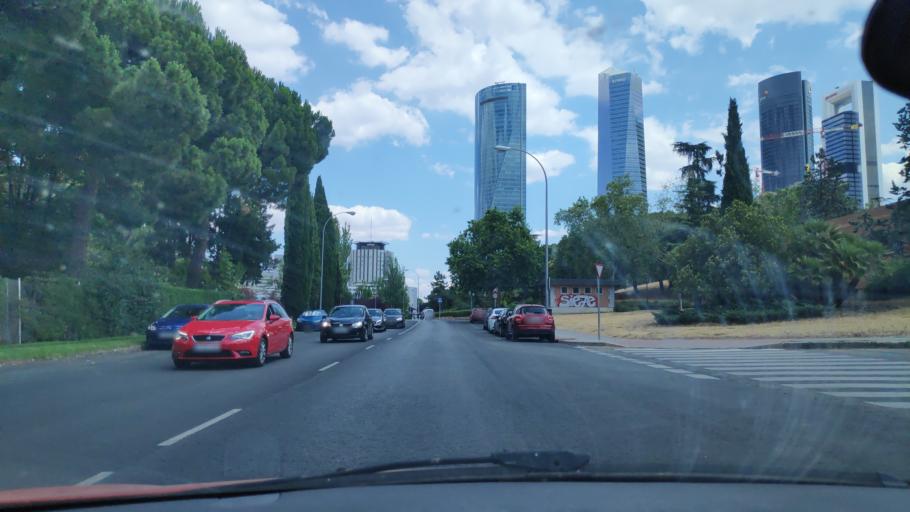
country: ES
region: Madrid
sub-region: Provincia de Madrid
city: Pinar de Chamartin
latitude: 40.4814
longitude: -3.6935
